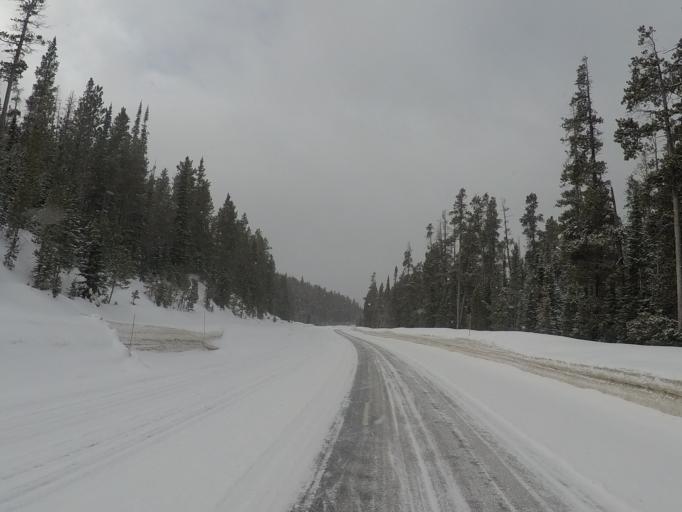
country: US
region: Montana
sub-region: Meagher County
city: White Sulphur Springs
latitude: 46.8493
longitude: -110.6894
